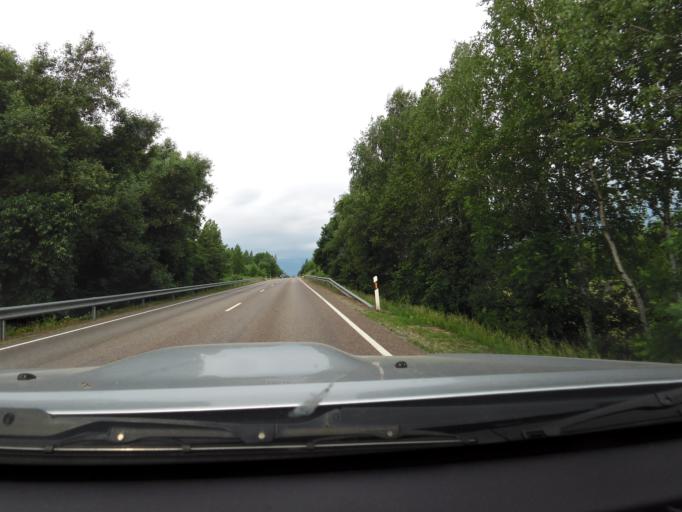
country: LT
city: Aukstadvaris
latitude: 54.5760
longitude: 24.4208
